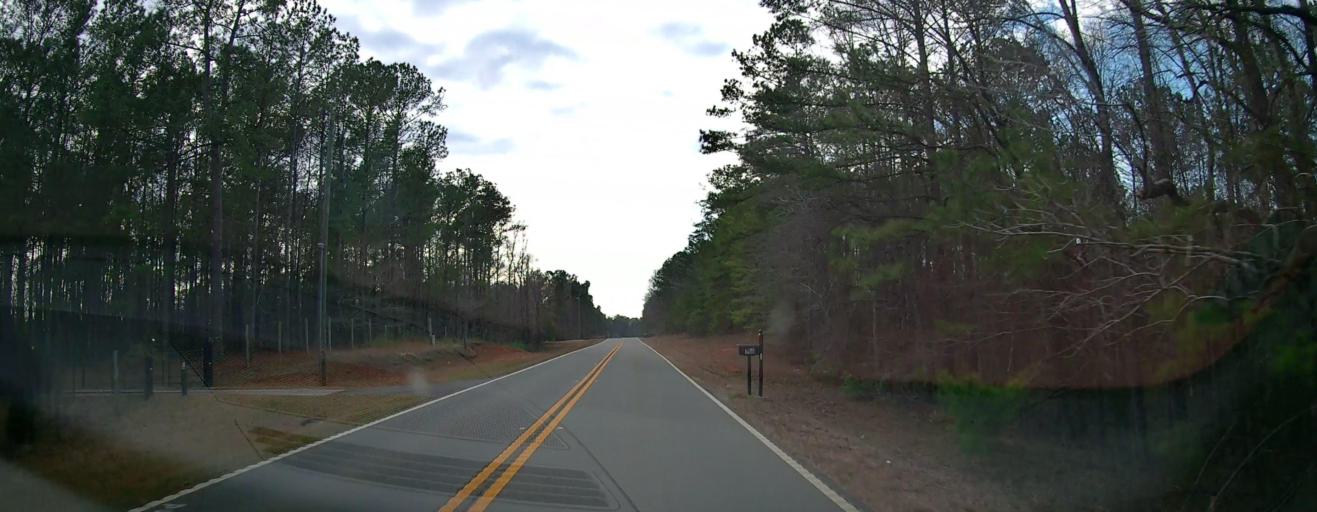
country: US
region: Georgia
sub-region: Harris County
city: Hamilton
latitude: 32.7017
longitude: -84.8465
